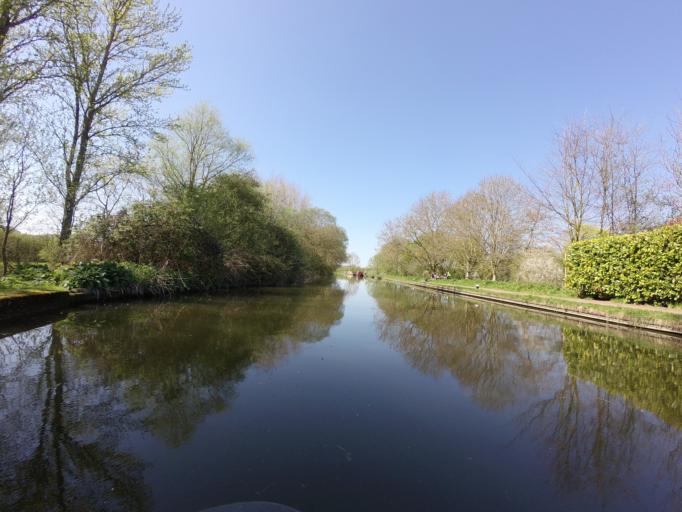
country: GB
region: England
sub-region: Hertfordshire
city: Berkhamsted
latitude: 51.7797
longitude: -0.6053
